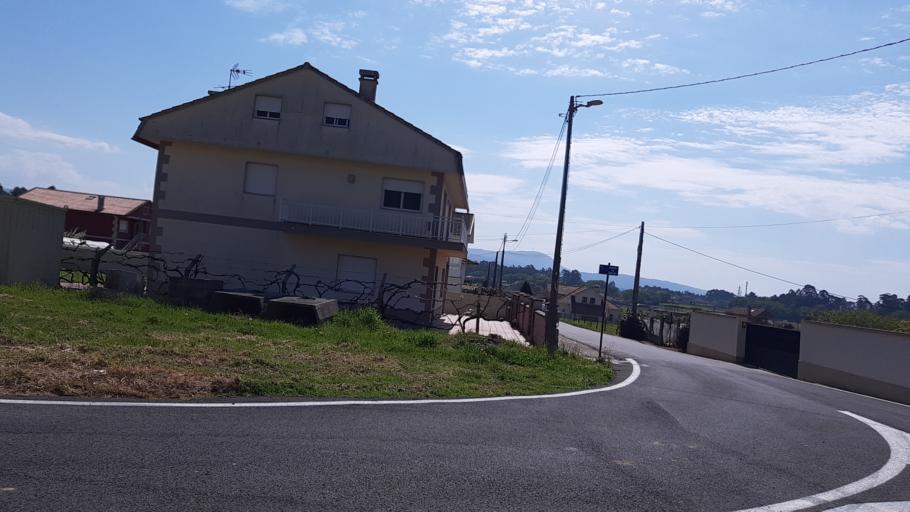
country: ES
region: Galicia
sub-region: Provincia de Pontevedra
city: O Rosal
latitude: 41.9378
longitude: -8.8539
